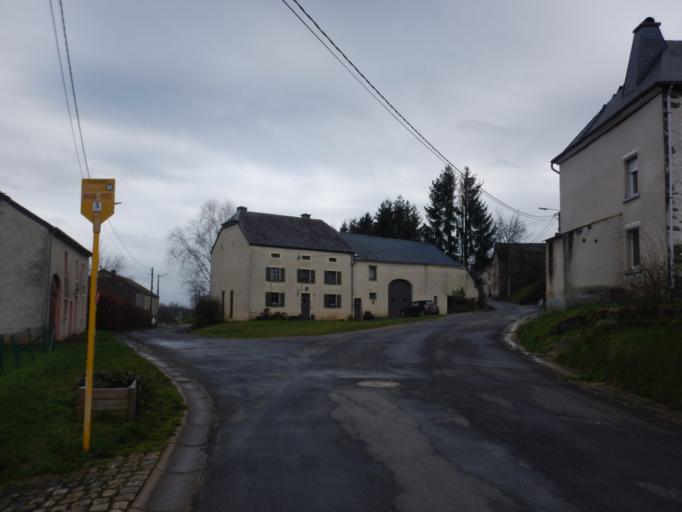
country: BE
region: Wallonia
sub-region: Province du Luxembourg
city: Attert
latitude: 49.7700
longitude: 5.7890
